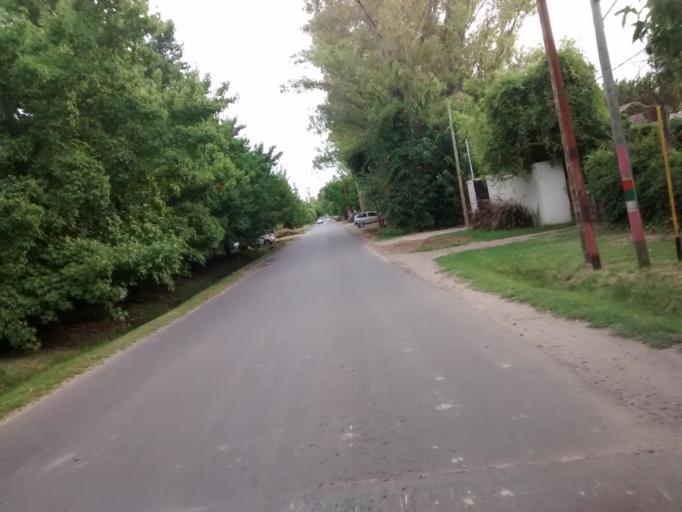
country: AR
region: Buenos Aires
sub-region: Partido de La Plata
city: La Plata
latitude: -34.8815
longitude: -58.0647
